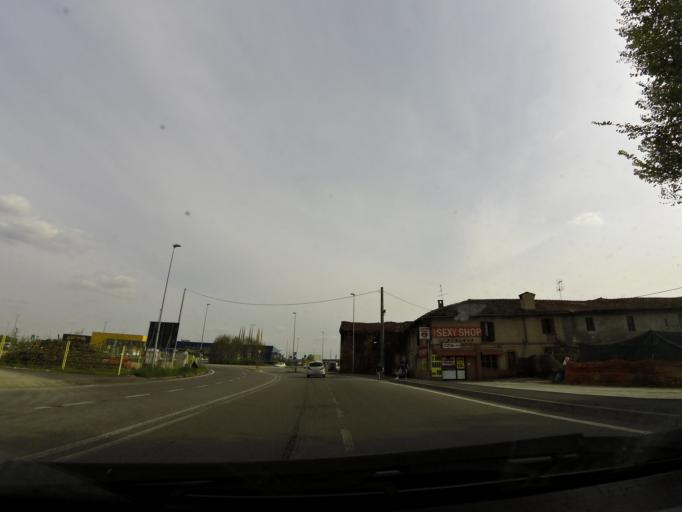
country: IT
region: Lombardy
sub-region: Citta metropolitana di Milano
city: Civesio
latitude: 45.3912
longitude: 9.2578
